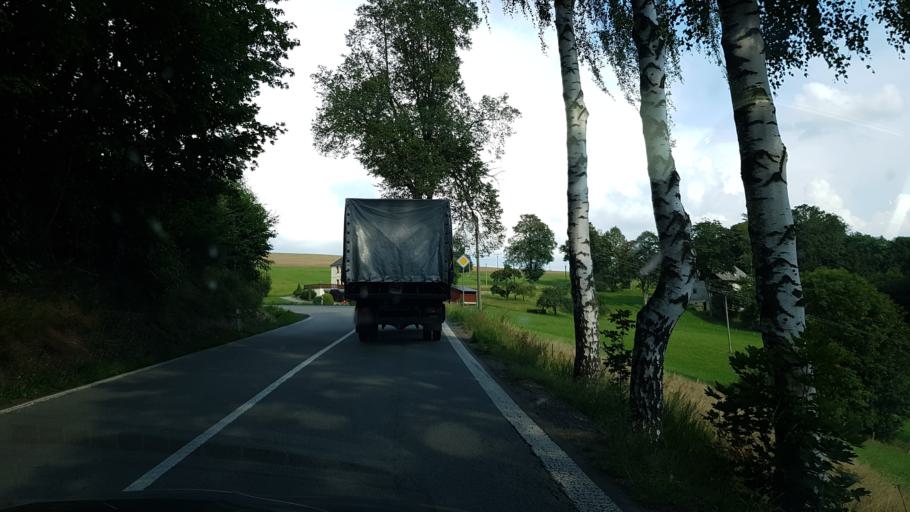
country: CZ
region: Pardubicky
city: Jablonne nad Orlici
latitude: 50.0944
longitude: 16.5767
